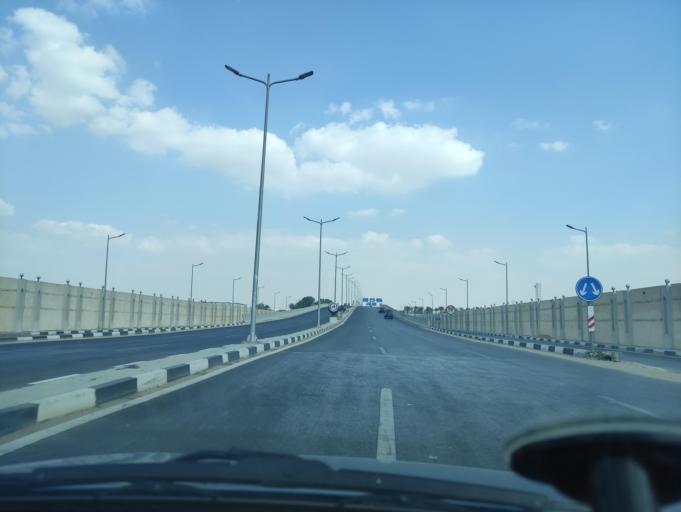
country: EG
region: Muhafazat al Qahirah
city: Cairo
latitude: 30.0412
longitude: 31.3005
